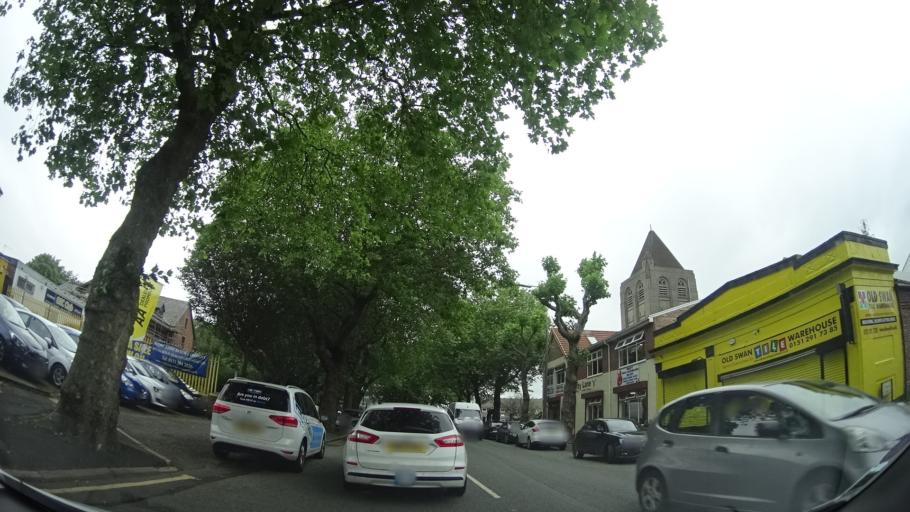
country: GB
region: England
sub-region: Liverpool
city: Liverpool
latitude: 53.4184
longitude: -2.9156
